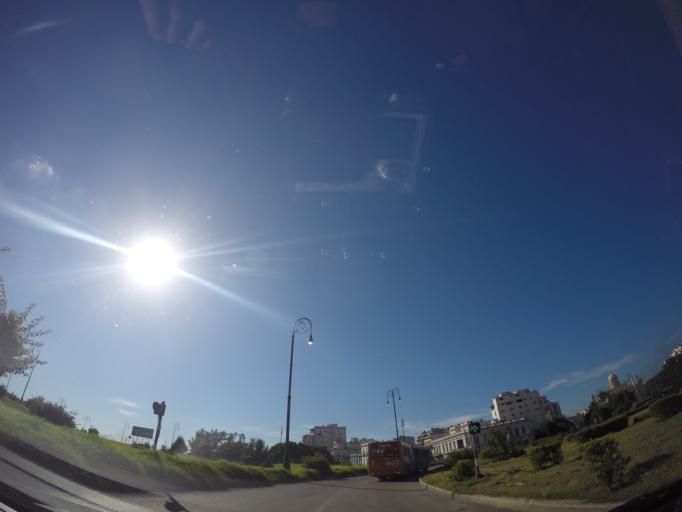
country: CU
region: La Habana
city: Centro Habana
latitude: 23.1449
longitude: -82.3555
